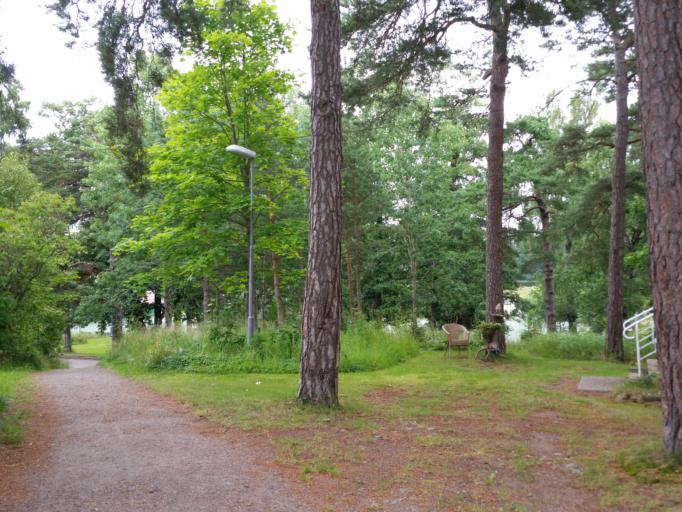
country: FI
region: Uusimaa
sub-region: Raaseporin
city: Hanko
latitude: 59.8242
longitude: 22.9742
